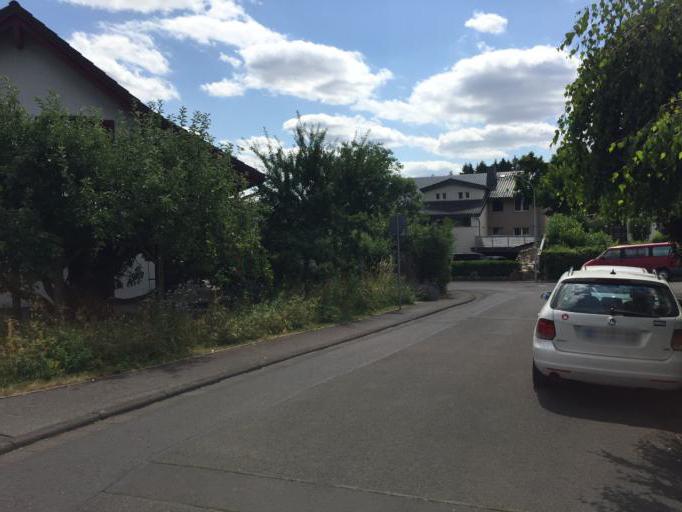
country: DE
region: Hesse
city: Lollar
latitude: 50.6484
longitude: 8.6746
